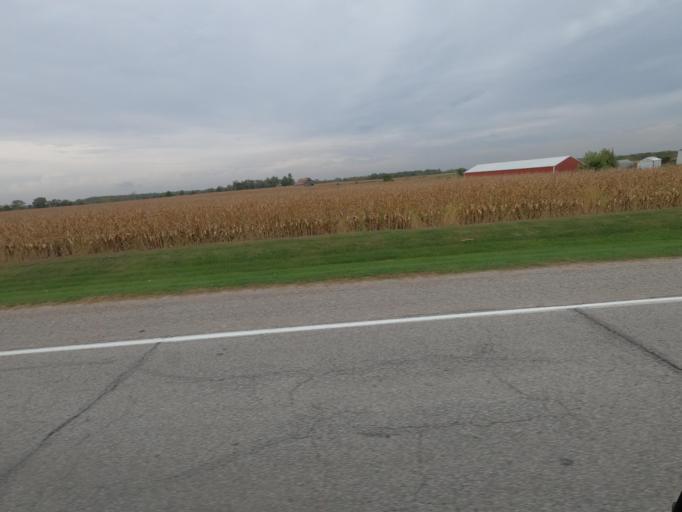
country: US
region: Iowa
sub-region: Van Buren County
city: Keosauqua
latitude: 40.8528
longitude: -92.0534
